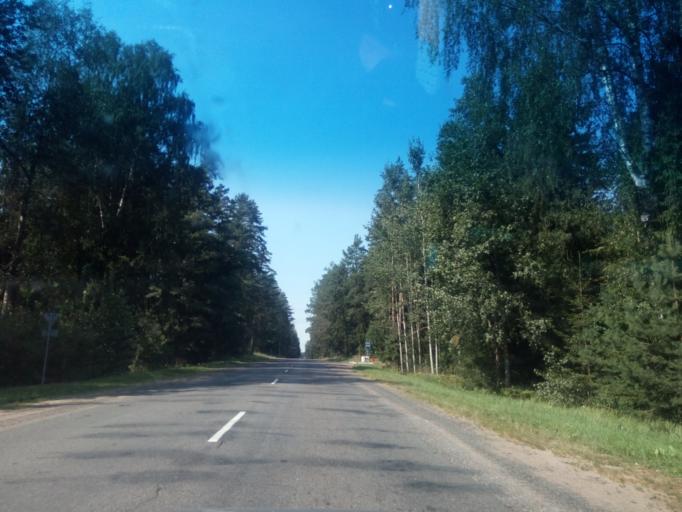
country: BY
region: Vitebsk
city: Vyerkhnyadzvinsk
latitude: 55.7930
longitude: 27.9687
